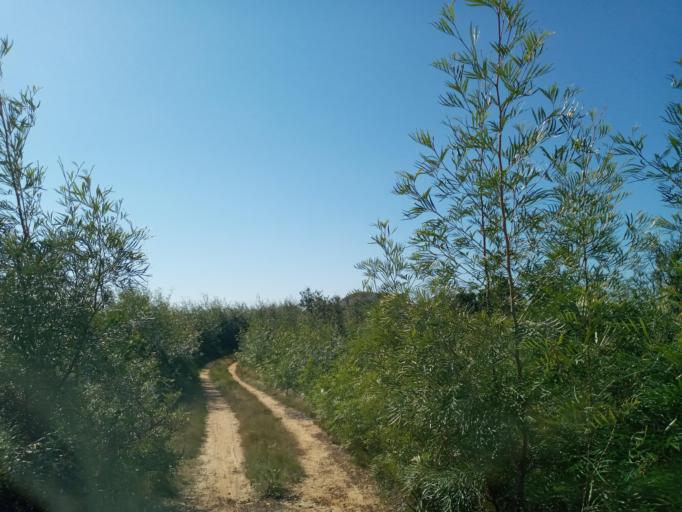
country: MG
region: Anosy
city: Fort Dauphin
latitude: -24.9117
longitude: 47.0895
